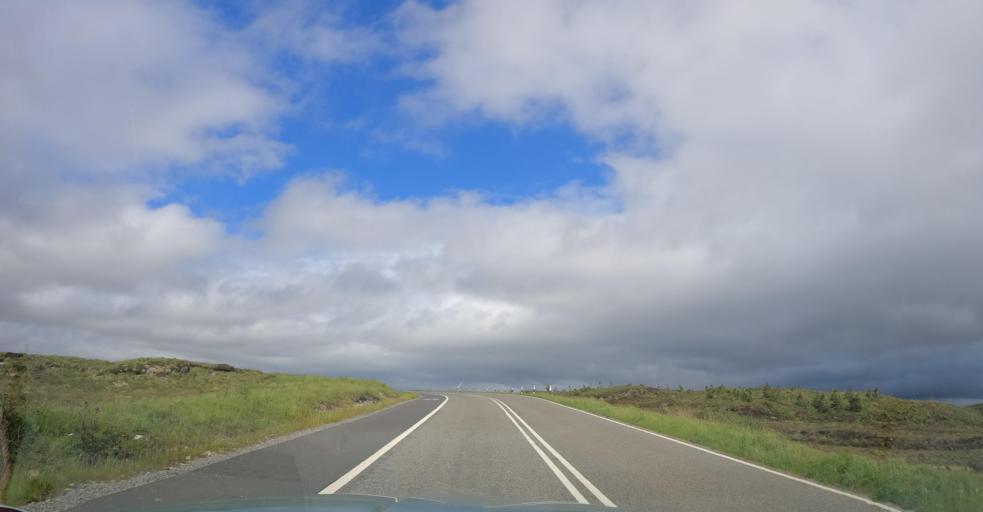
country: GB
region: Scotland
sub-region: Eilean Siar
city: Stornoway
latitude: 58.1899
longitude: -6.4393
